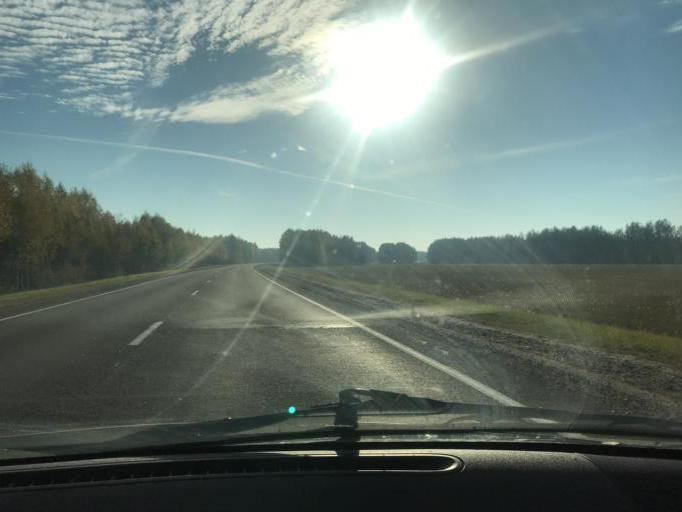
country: BY
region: Brest
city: Drahichyn
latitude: 52.1863
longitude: 25.2901
